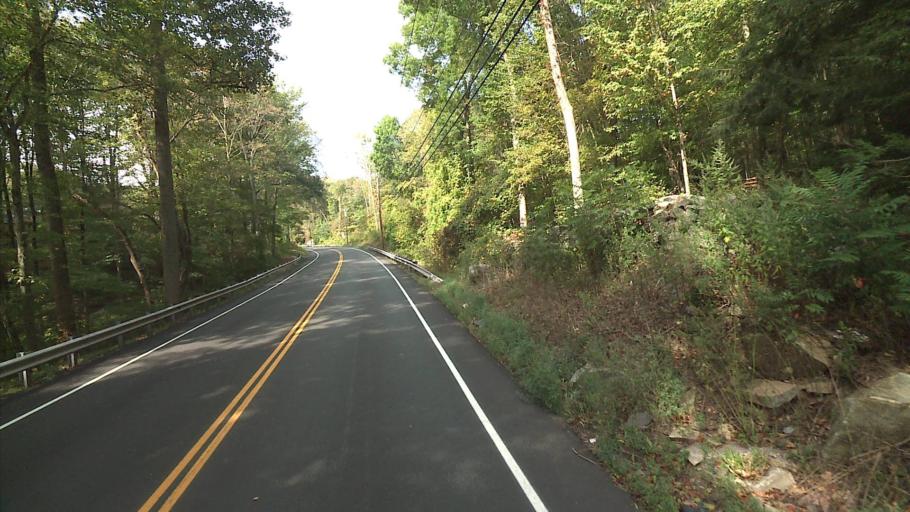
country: US
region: Connecticut
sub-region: New Haven County
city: Oxford
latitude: 41.3892
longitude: -73.1955
